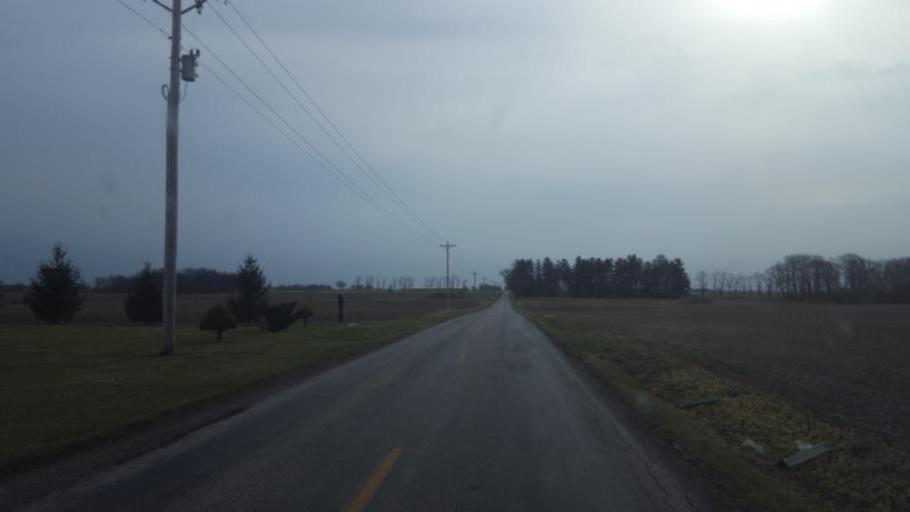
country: US
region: Ohio
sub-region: Marion County
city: Marion
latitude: 40.6740
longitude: -83.0368
